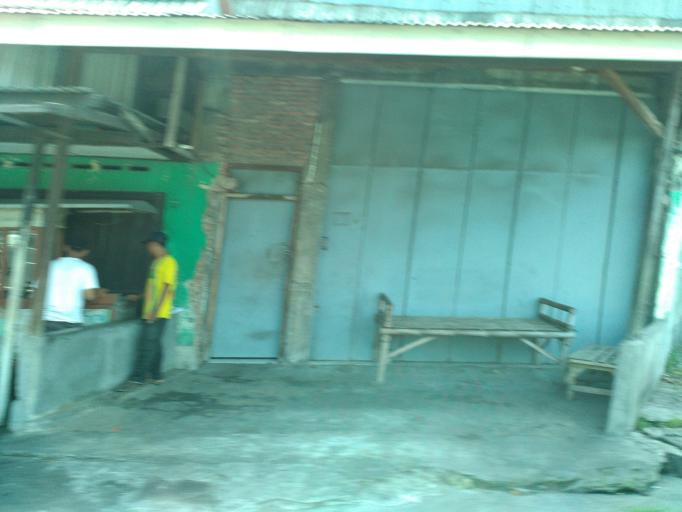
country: ID
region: Central Java
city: Jogonalan
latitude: -7.7312
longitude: 110.5456
